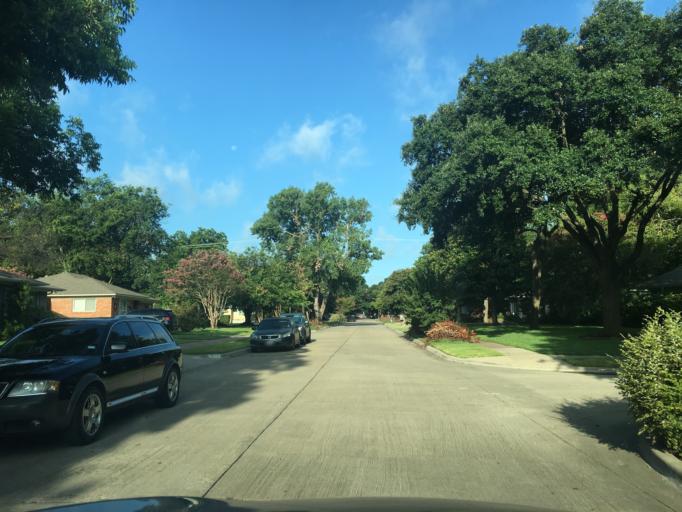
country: US
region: Texas
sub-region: Dallas County
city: Highland Park
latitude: 32.8464
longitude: -96.7488
